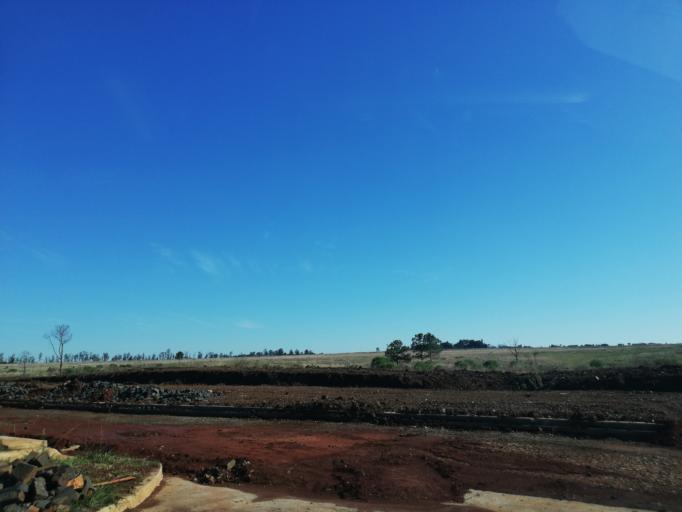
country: AR
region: Misiones
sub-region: Departamento de Capital
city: Posadas
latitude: -27.4066
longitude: -55.9959
